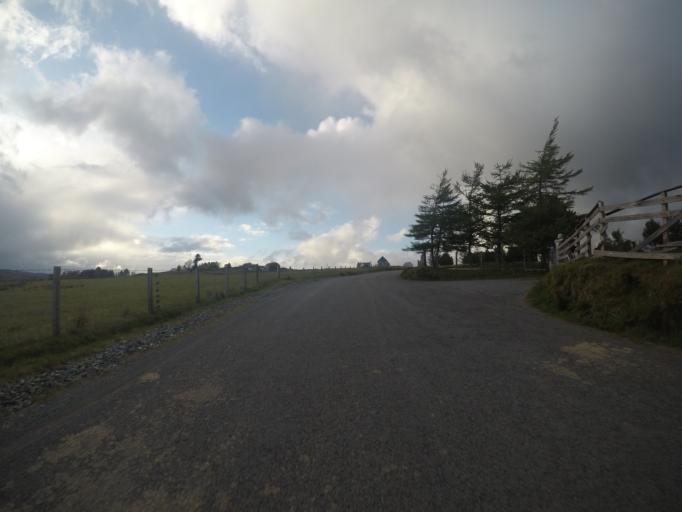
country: GB
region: Scotland
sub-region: Highland
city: Isle of Skye
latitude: 57.4550
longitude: -6.2980
